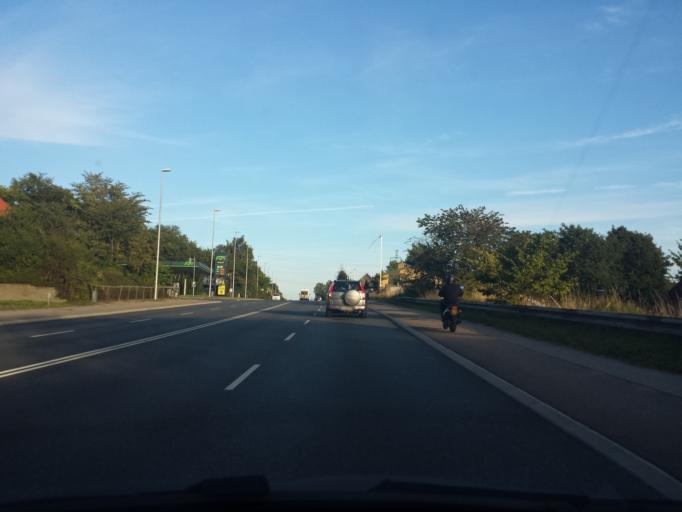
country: DK
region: Capital Region
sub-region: Egedal Kommune
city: Stenlose
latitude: 55.7674
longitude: 12.2050
